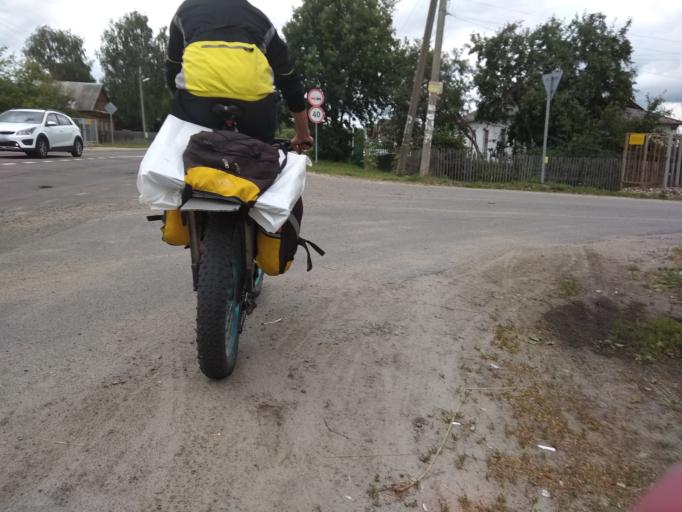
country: RU
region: Moskovskaya
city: Misheronskiy
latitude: 55.5993
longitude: 39.7052
